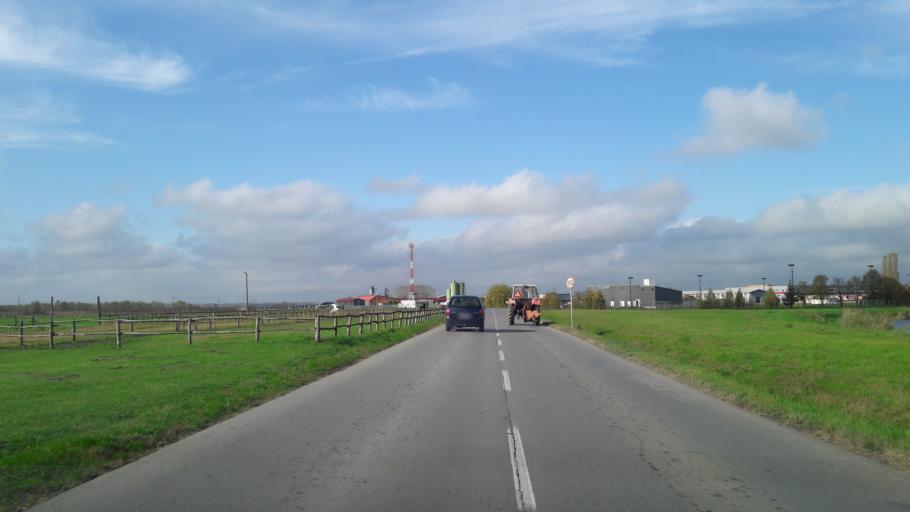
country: HR
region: Osjecko-Baranjska
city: Darda
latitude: 45.6196
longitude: 18.6875
